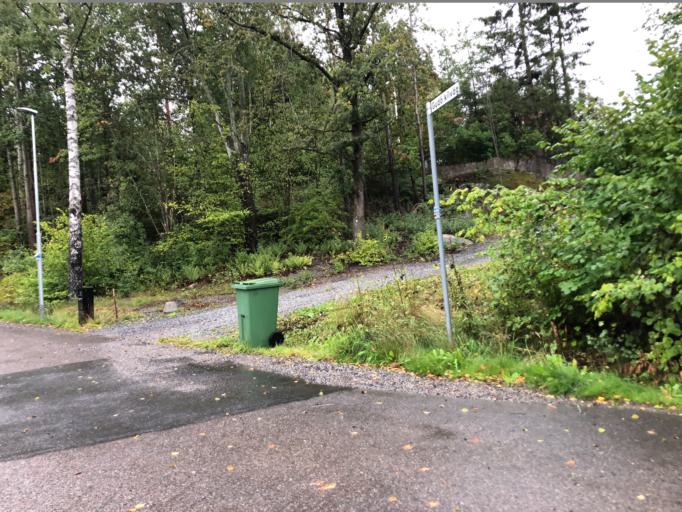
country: SE
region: Stockholm
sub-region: Tyreso Kommun
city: Bollmora
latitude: 59.2083
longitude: 18.2083
